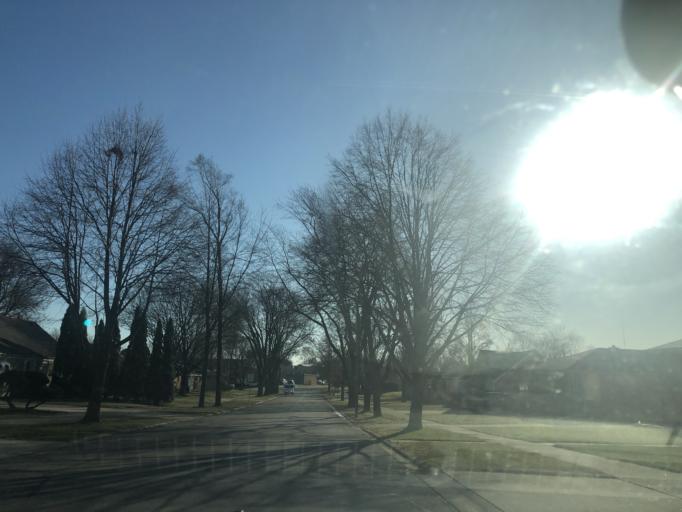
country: US
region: Illinois
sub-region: DuPage County
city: Addison
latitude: 41.9390
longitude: -87.9986
